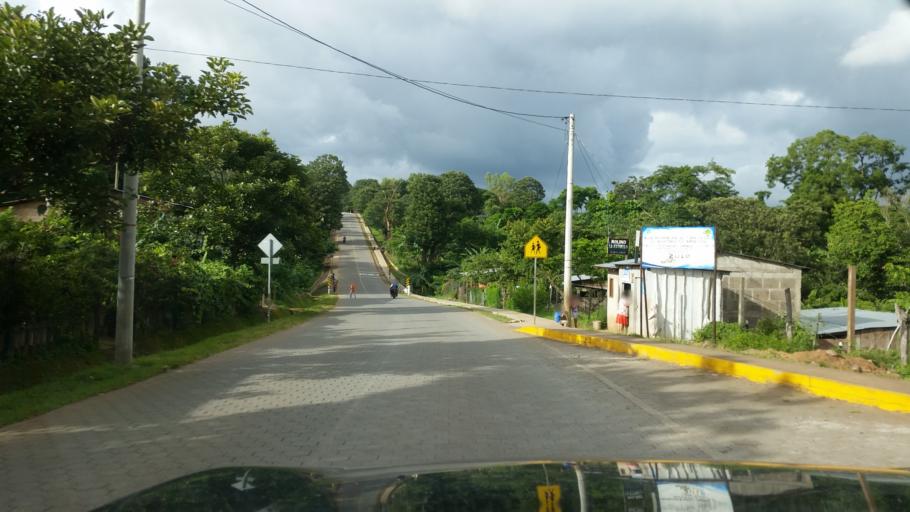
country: NI
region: Matagalpa
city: San Ramon
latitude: 13.1632
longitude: -85.7292
